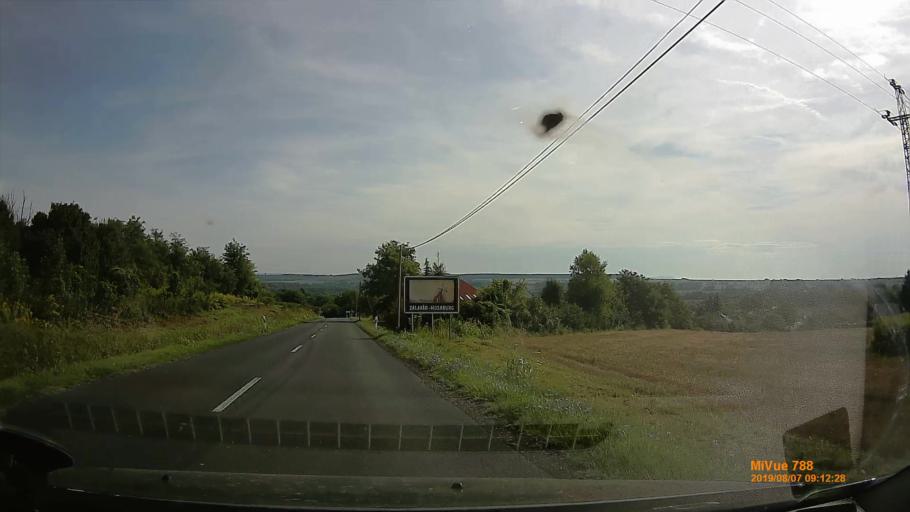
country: HU
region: Zala
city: Sarmellek
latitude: 46.7222
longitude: 17.1038
